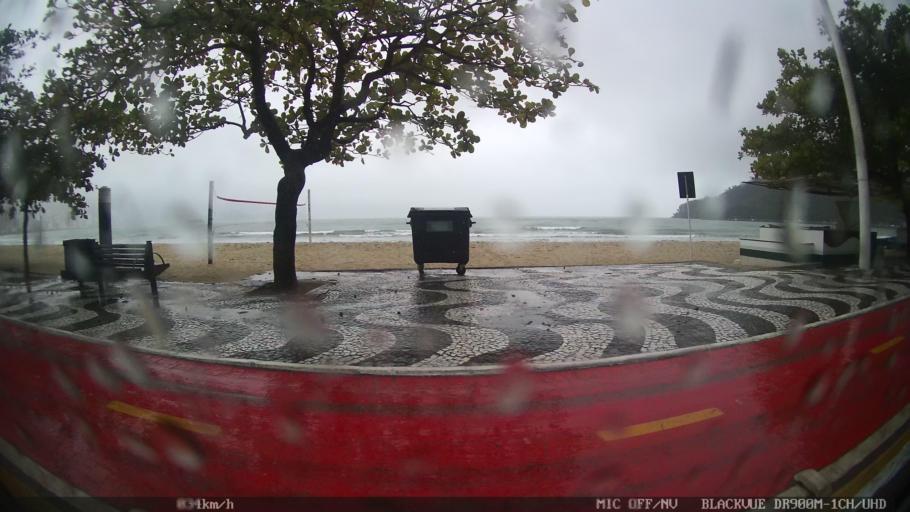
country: BR
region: Santa Catarina
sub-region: Balneario Camboriu
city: Balneario Camboriu
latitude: -27.0061
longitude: -48.6097
